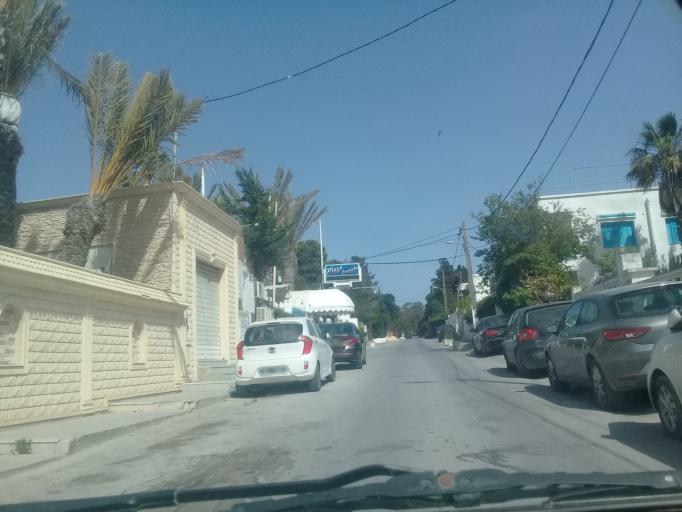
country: TN
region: Tunis
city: Al Marsa
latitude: 36.8815
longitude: 10.3366
